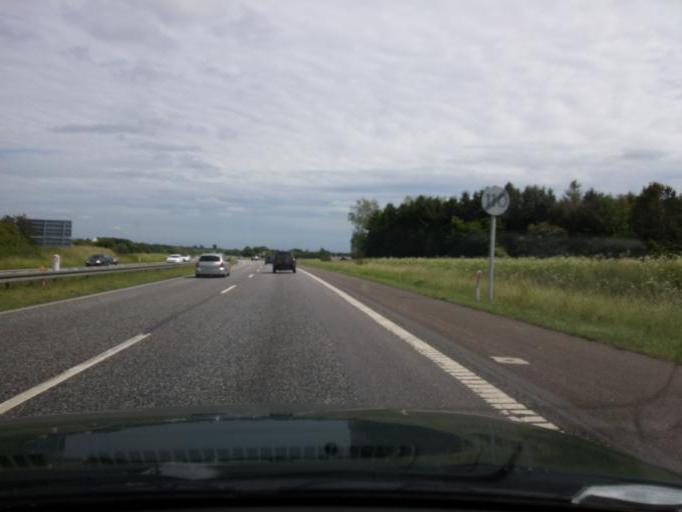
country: DK
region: South Denmark
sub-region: Middelfart Kommune
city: Norre Aby
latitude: 55.4647
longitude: 9.9050
